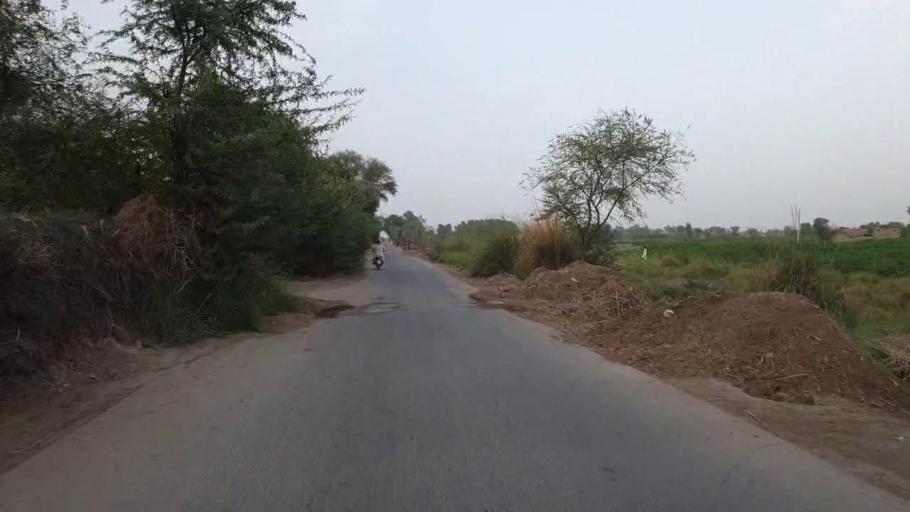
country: PK
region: Sindh
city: Daur
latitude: 26.4210
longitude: 68.2512
